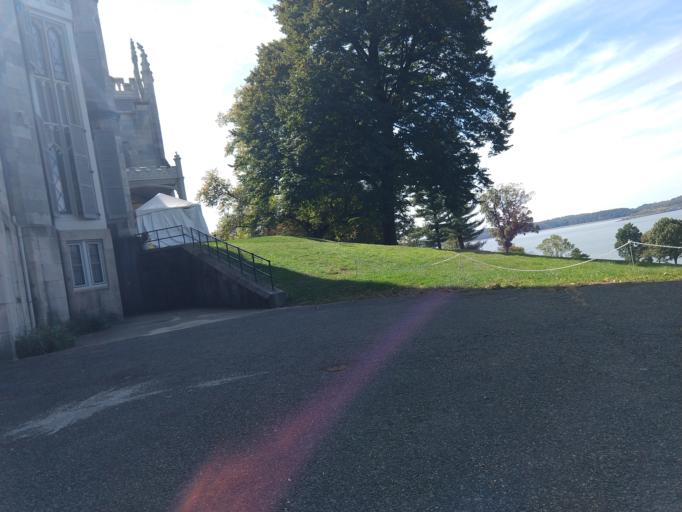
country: US
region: New York
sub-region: Westchester County
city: Irvington
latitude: 41.0543
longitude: -73.8674
